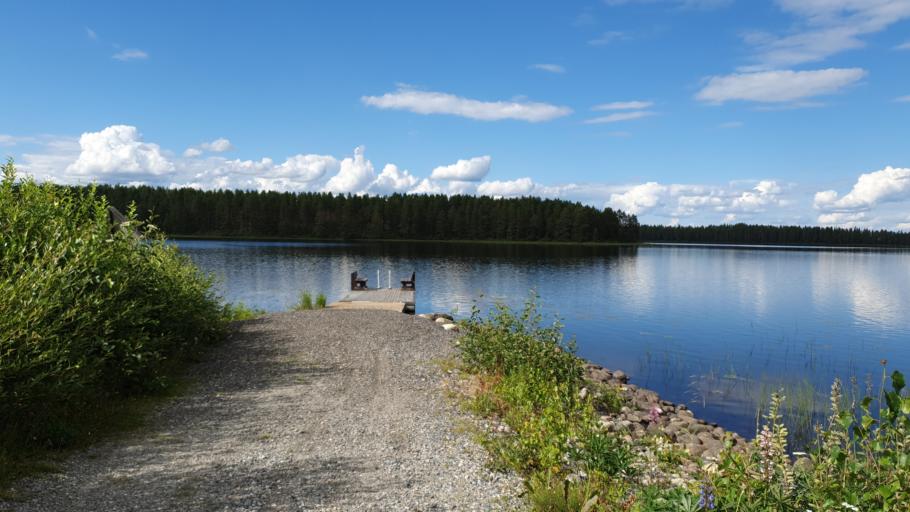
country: FI
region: Kainuu
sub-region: Kehys-Kainuu
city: Kuhmo
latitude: 64.1346
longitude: 29.5300
